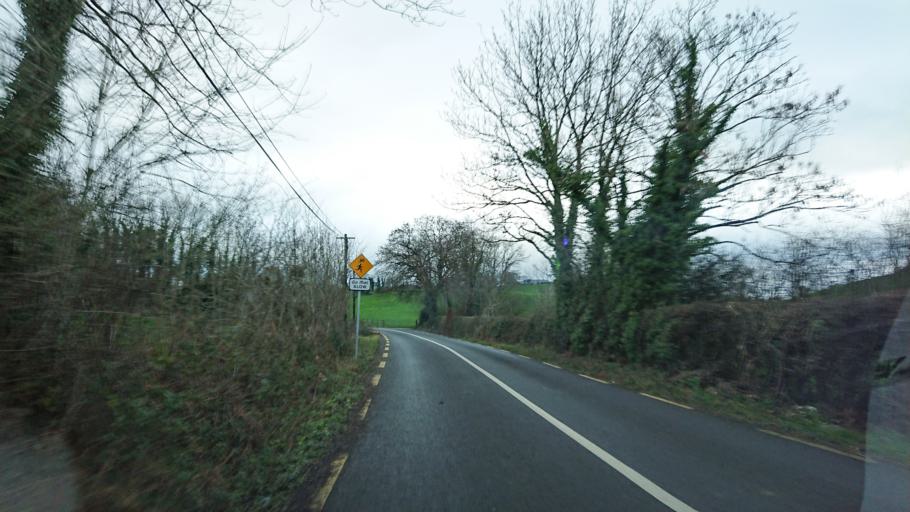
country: IE
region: Munster
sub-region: Waterford
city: Portlaw
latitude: 52.2691
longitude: -7.3966
